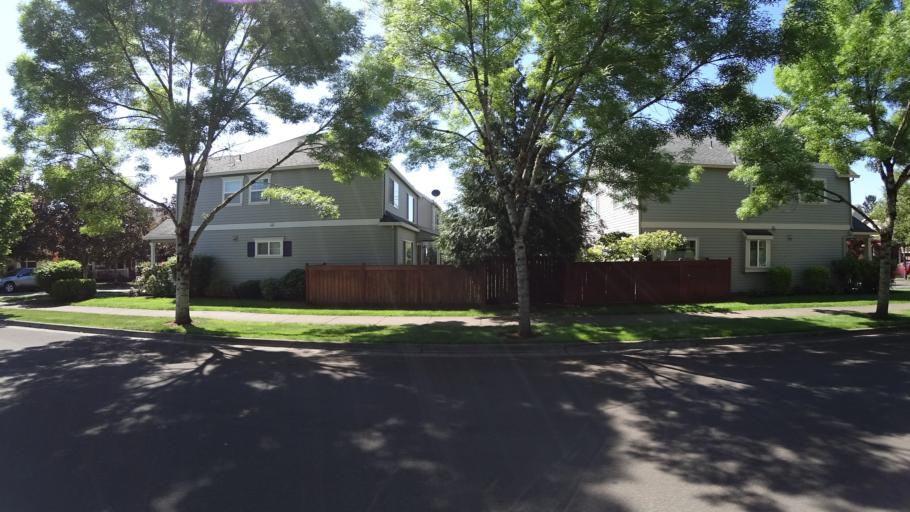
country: US
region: Oregon
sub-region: Washington County
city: Rockcreek
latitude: 45.5268
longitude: -122.9180
